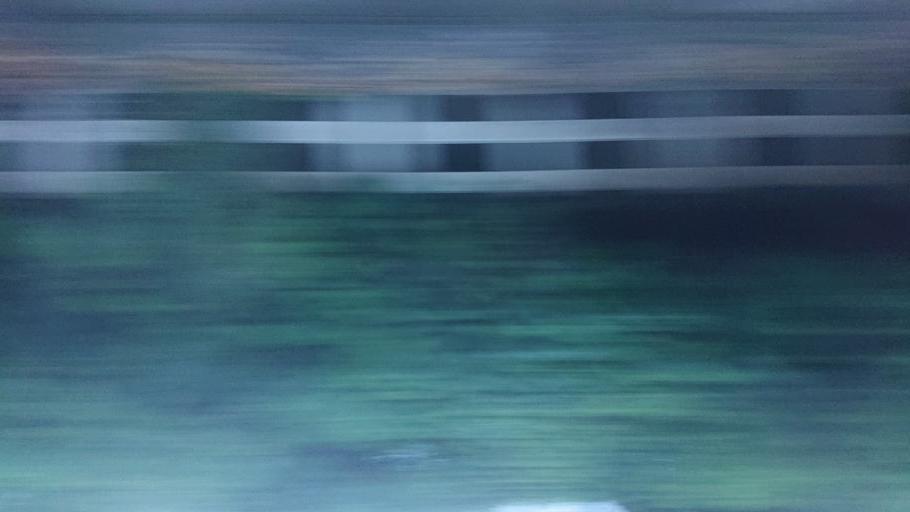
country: TW
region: Taiwan
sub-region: Taitung
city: Taitung
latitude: 23.0384
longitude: 121.1621
